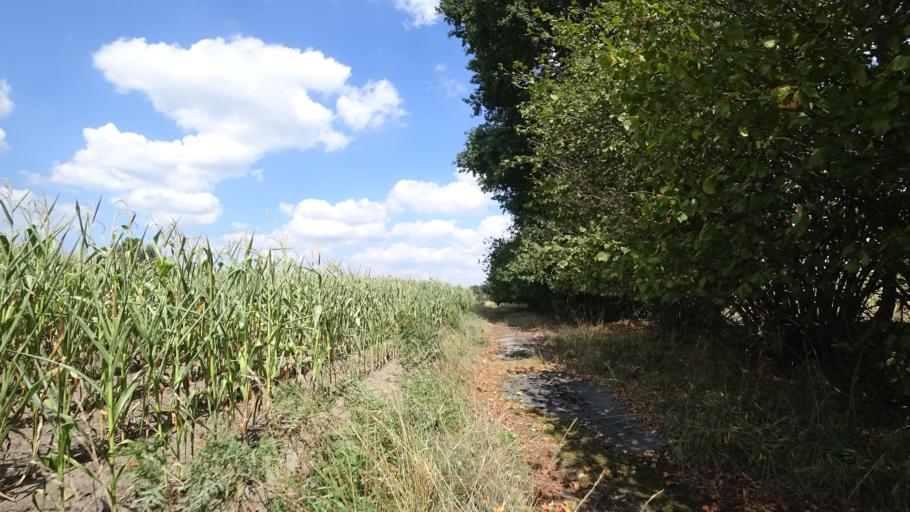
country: DE
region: North Rhine-Westphalia
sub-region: Regierungsbezirk Detmold
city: Rheda-Wiedenbruck
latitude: 51.8797
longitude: 8.2904
